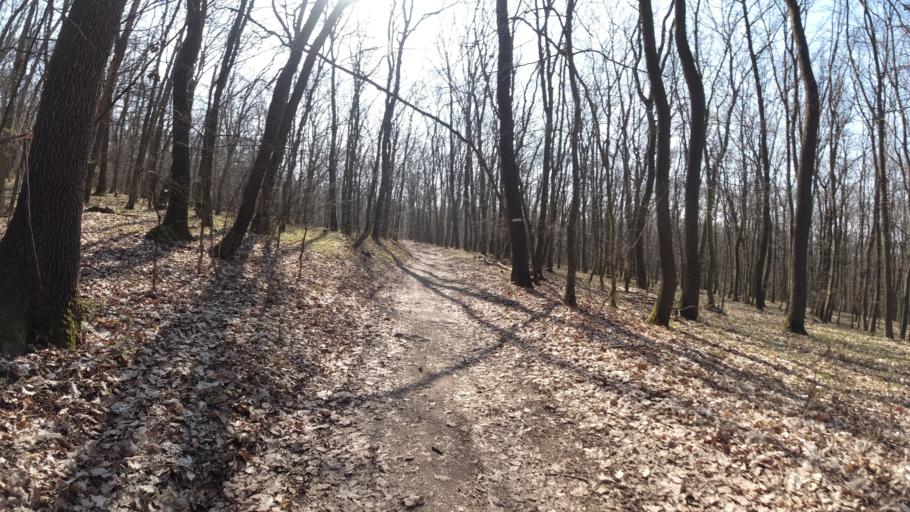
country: SK
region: Trnavsky
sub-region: Okres Trnava
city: Piestany
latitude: 48.5617
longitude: 17.8707
